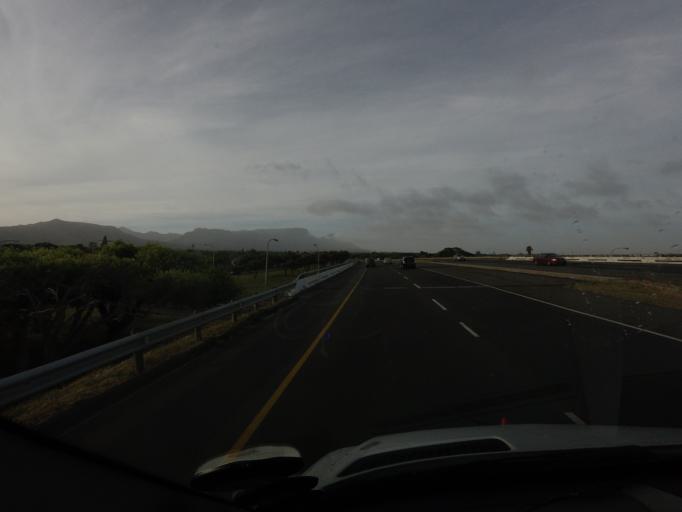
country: ZA
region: Western Cape
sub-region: City of Cape Town
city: Bergvliet
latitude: -34.0648
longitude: 18.4487
